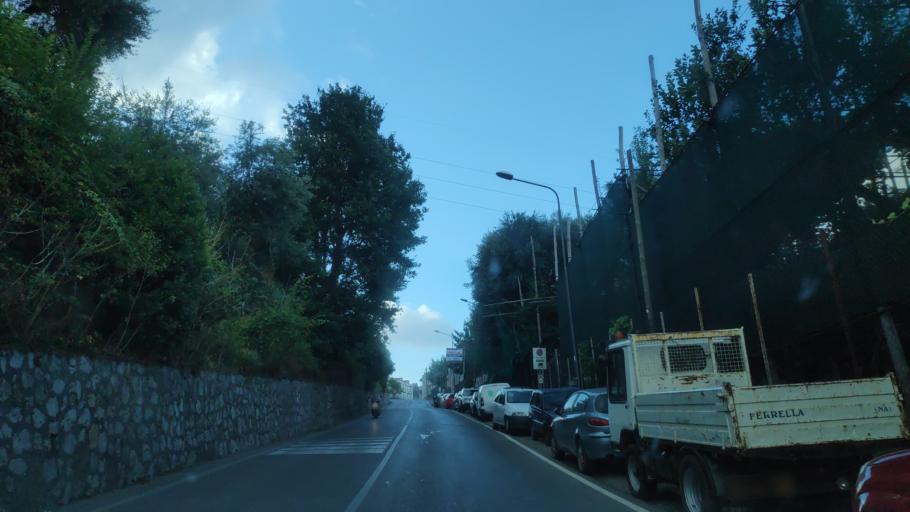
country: IT
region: Campania
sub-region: Provincia di Napoli
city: Piano di Sorrento
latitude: 40.6300
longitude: 14.4208
